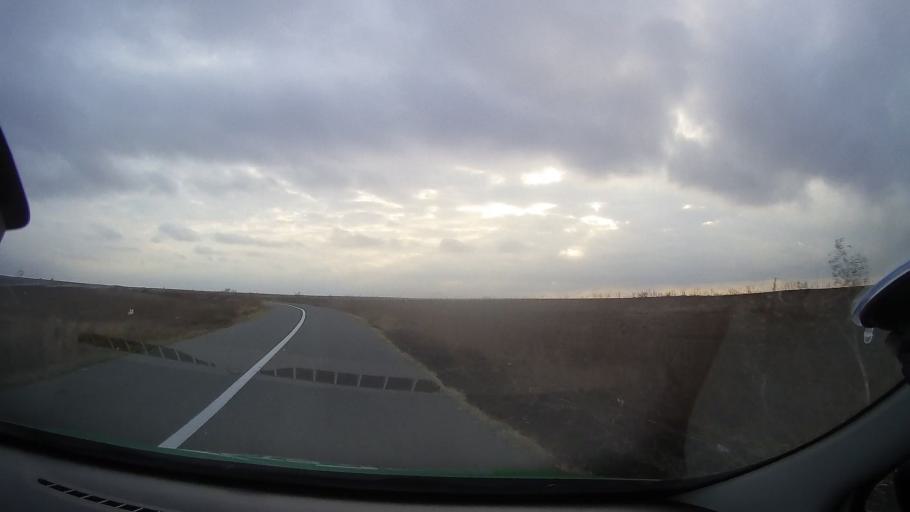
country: RO
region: Constanta
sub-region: Comuna Pestera
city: Pestera
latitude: 44.1520
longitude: 28.1140
